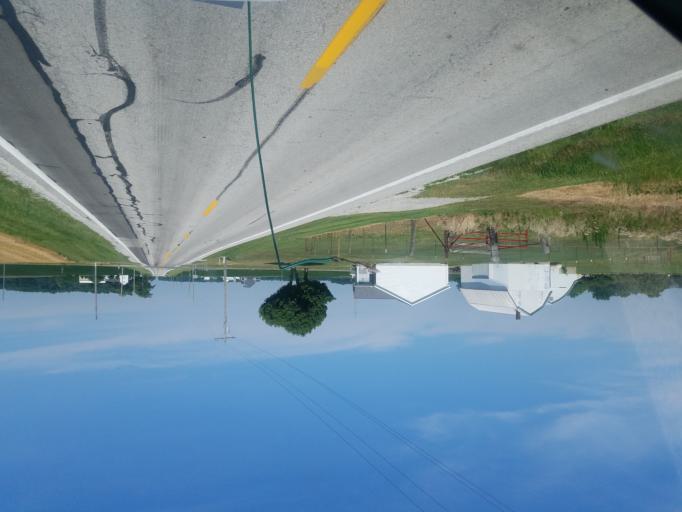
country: US
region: Ohio
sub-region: Shelby County
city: Botkins
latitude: 40.4968
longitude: -84.2122
